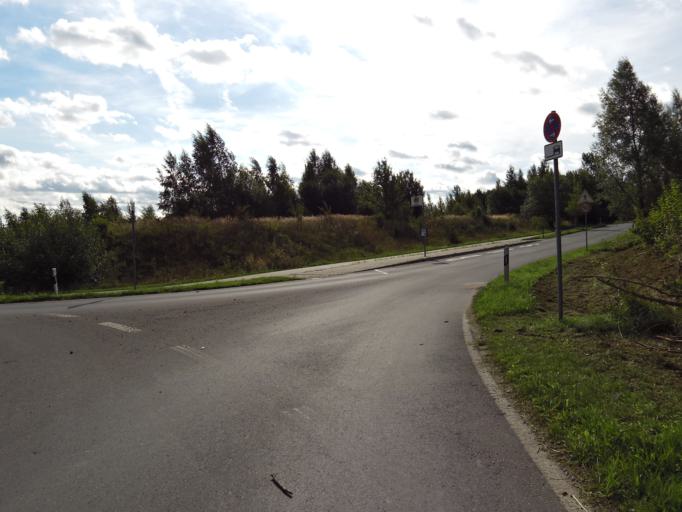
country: DE
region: North Rhine-Westphalia
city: Niedermerz
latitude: 50.8523
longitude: 6.2639
